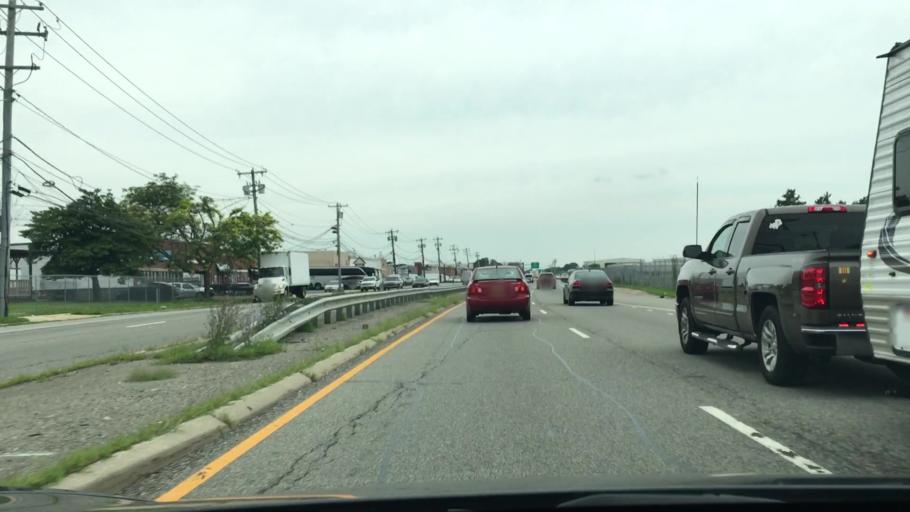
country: US
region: New York
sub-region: Suffolk County
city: East Farmingdale
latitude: 40.7187
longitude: -73.4107
